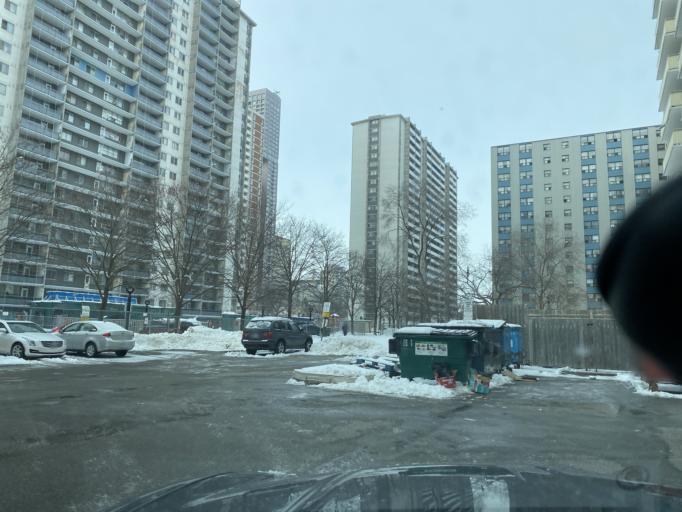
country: CA
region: Ontario
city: Toronto
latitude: 43.6693
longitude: -79.3733
